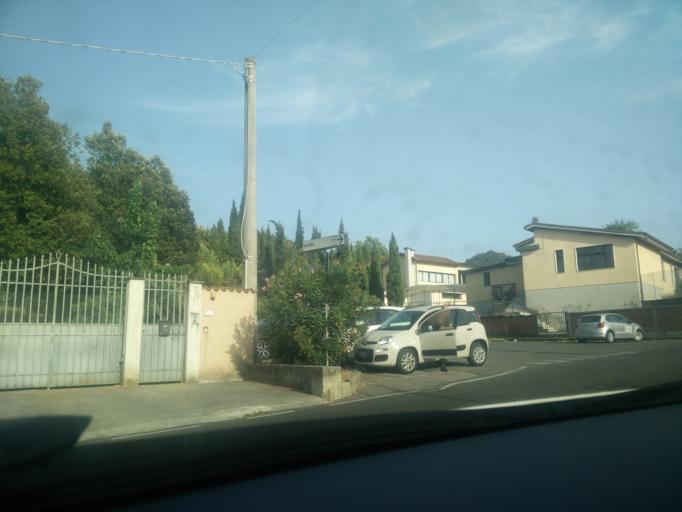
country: IT
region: Tuscany
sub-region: Provincia di Massa-Carrara
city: Carrara
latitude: 44.0584
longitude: 10.0862
